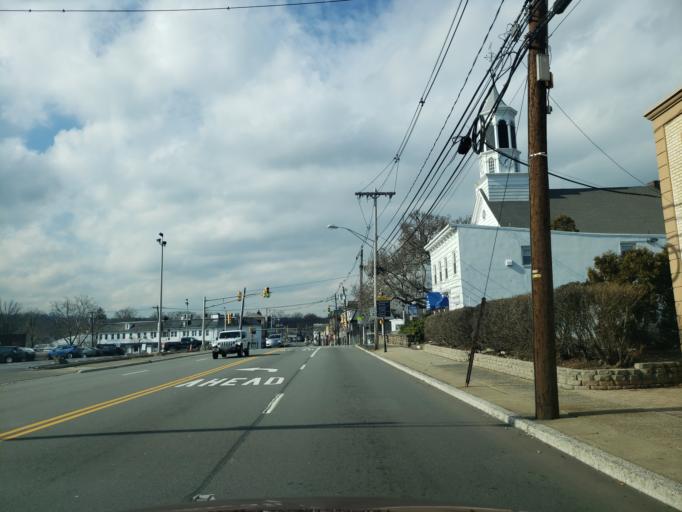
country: US
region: New Jersey
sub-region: Union County
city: Springfield
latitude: 40.7109
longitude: -74.3097
